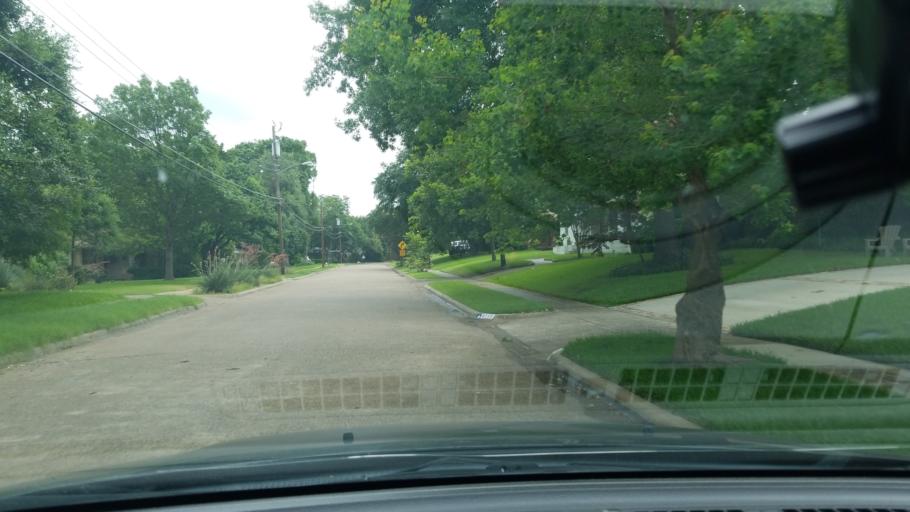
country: US
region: Texas
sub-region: Dallas County
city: Highland Park
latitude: 32.8131
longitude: -96.6949
